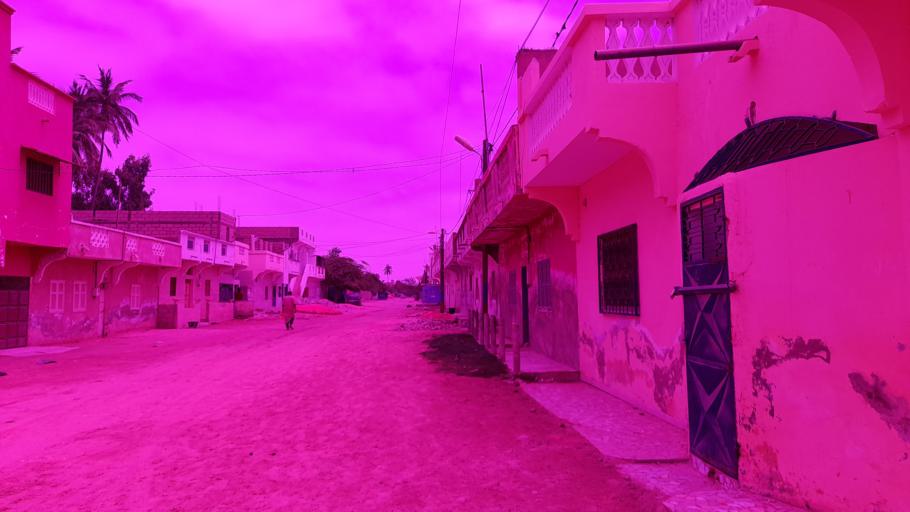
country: SN
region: Saint-Louis
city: Saint-Louis
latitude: 16.0158
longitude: -16.4867
